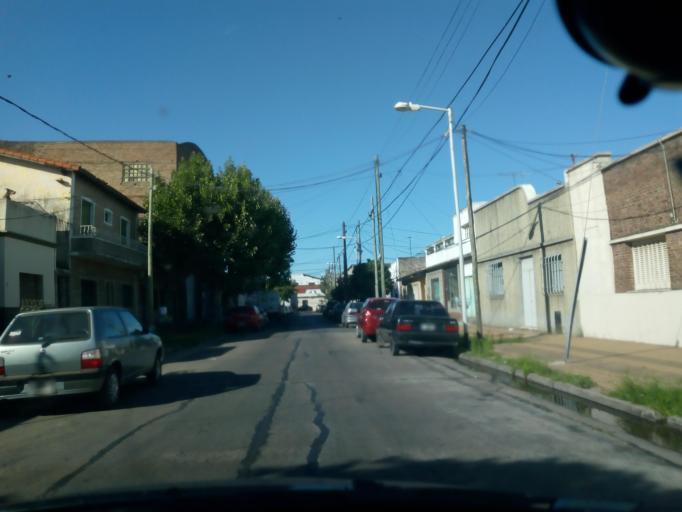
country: AR
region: Buenos Aires
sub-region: Partido de Avellaneda
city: Avellaneda
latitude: -34.6778
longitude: -58.3529
